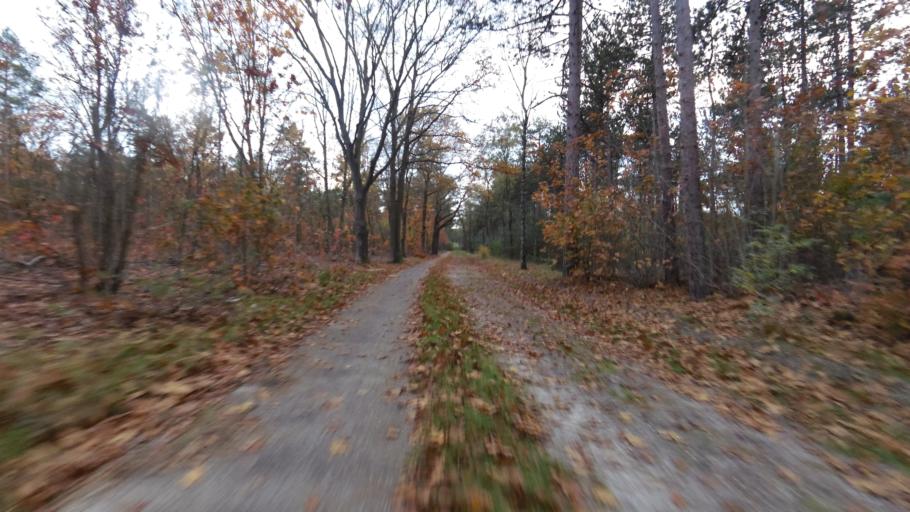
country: NL
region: Gelderland
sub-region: Gemeente Nunspeet
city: Nunspeet
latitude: 52.3792
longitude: 5.8358
